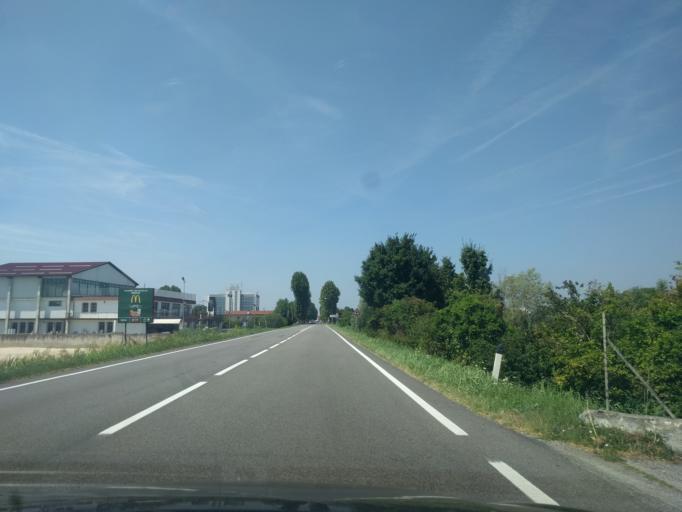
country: IT
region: Veneto
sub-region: Provincia di Padova
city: Stanghella
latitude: 45.1277
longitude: 11.7629
